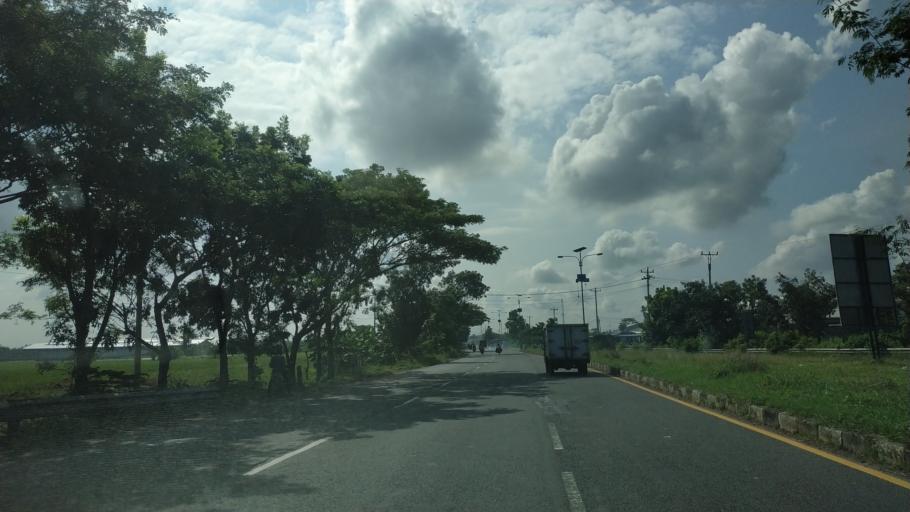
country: ID
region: Central Java
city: Comal
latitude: -6.9004
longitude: 109.5097
